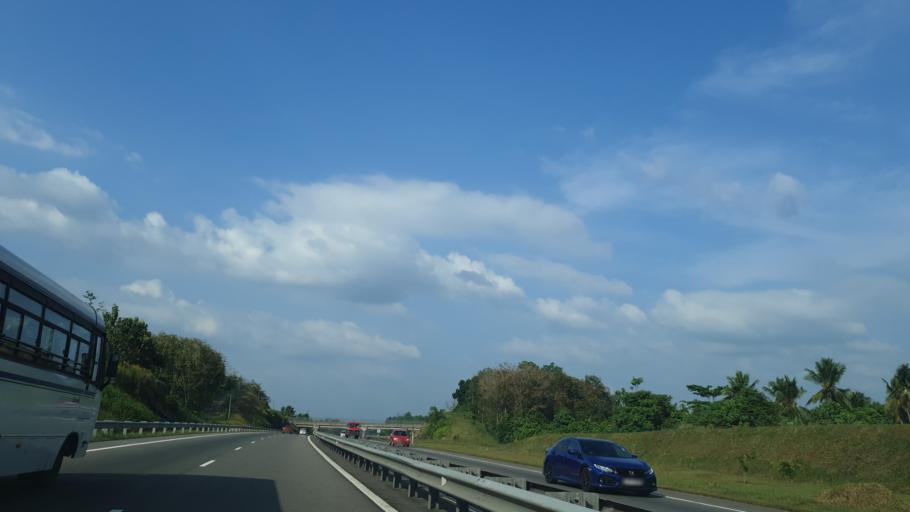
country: LK
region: Western
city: Horana South
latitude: 6.6636
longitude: 80.0026
